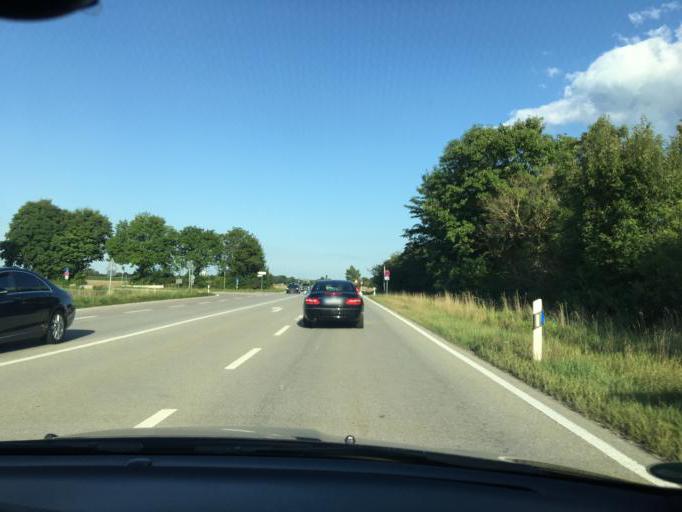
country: DE
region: Bavaria
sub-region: Upper Bavaria
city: Unterfoehring
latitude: 48.1824
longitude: 11.6712
